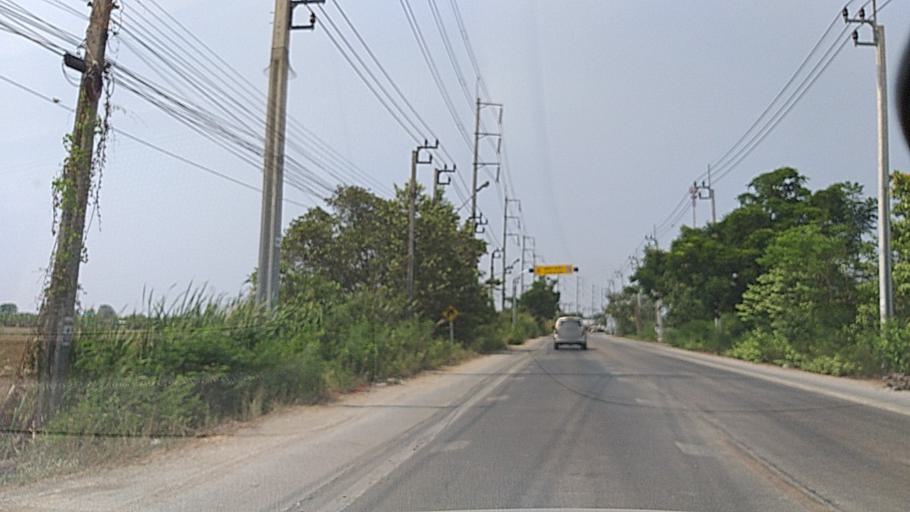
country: TH
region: Nonthaburi
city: Sai Noi
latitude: 13.9411
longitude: 100.3158
